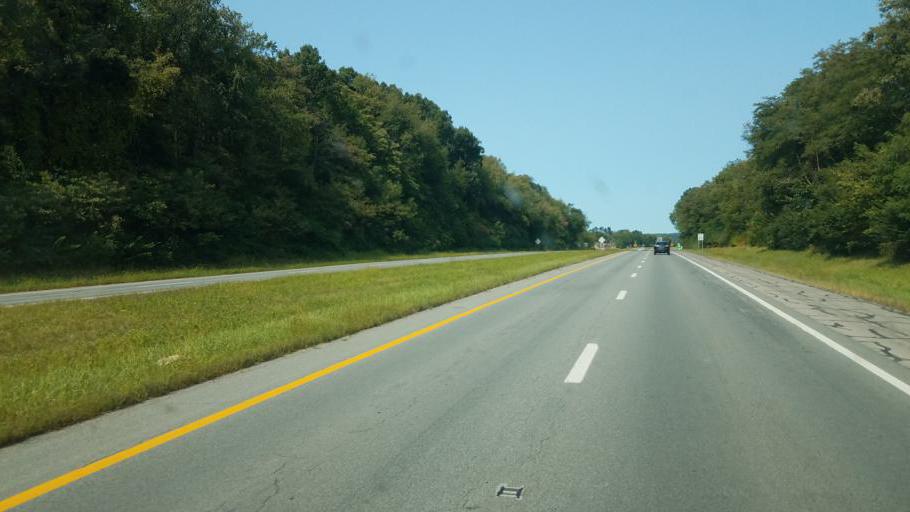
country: US
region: Ohio
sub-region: Wayne County
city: Wooster
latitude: 40.7741
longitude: -81.9713
